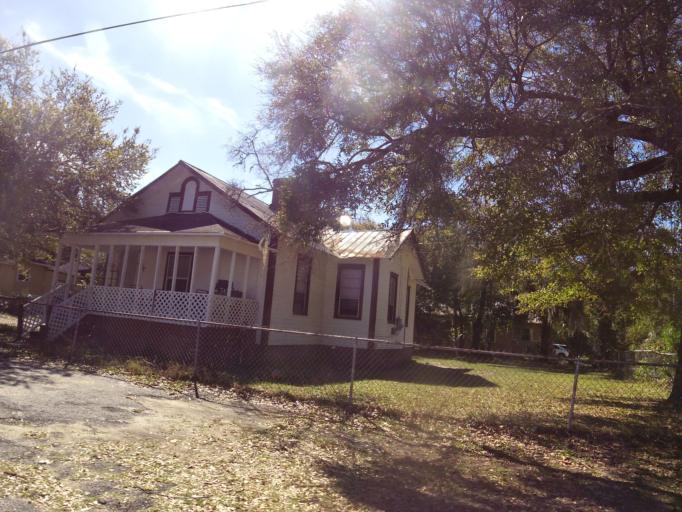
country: US
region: Florida
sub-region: Duval County
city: Jacksonville
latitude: 30.3629
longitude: -81.6434
